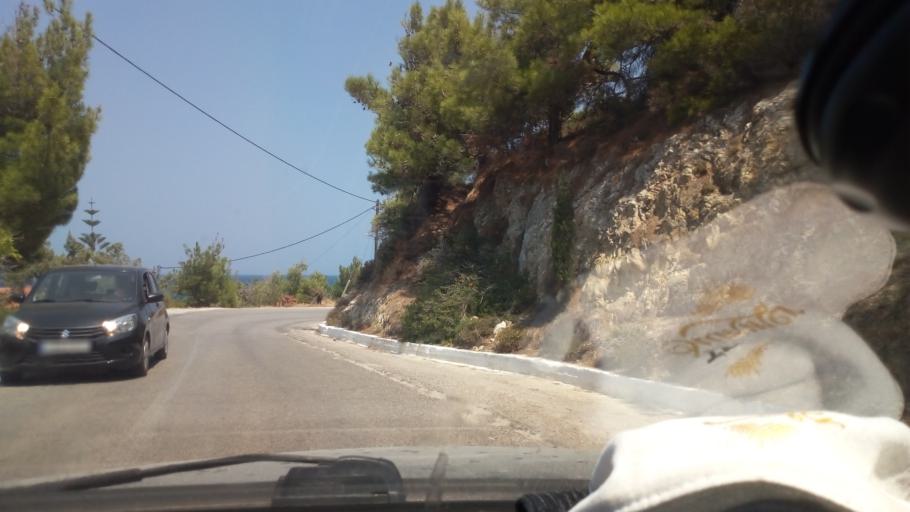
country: GR
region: North Aegean
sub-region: Nomos Samou
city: Agios Kirykos
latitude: 37.6302
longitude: 26.1045
